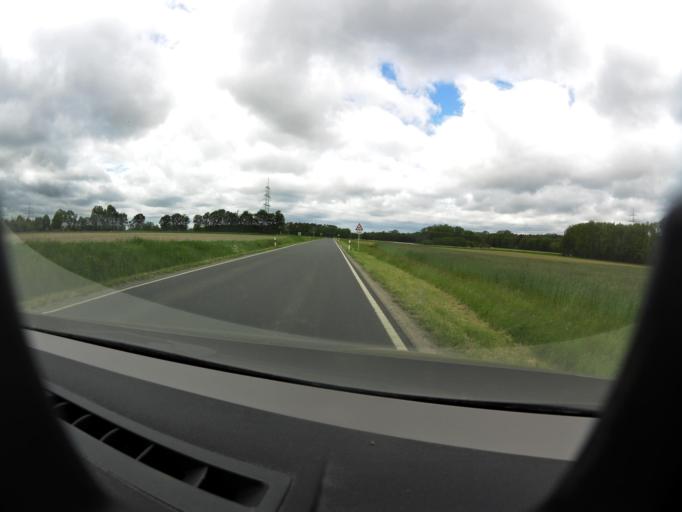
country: DE
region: Bavaria
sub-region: Regierungsbezirk Unterfranken
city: Wiesentheid
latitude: 49.7934
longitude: 10.3304
